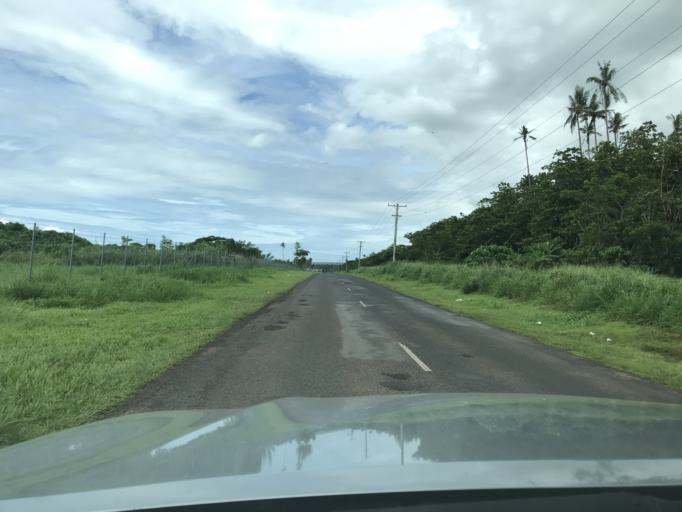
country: WS
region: A'ana
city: Satapuala
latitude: -13.8338
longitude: -172.0042
